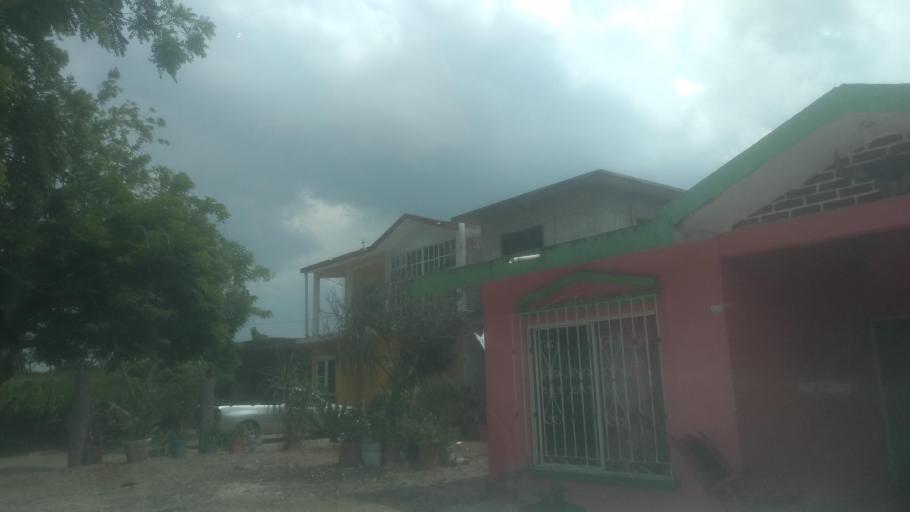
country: MX
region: Veracruz
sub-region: Emiliano Zapata
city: Plan del Rio
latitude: 19.4301
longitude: -96.6990
